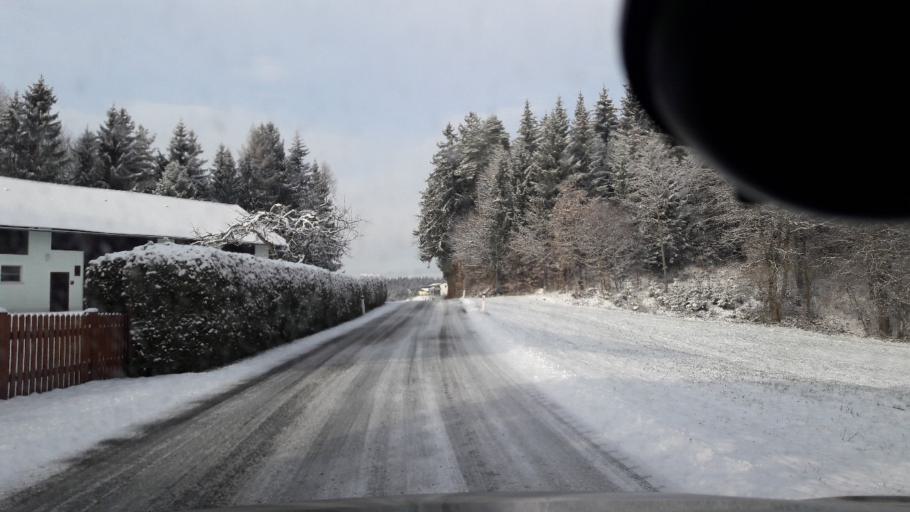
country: AT
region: Styria
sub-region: Politischer Bezirk Graz-Umgebung
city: Sankt Oswald bei Plankenwarth
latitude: 47.0921
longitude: 15.2572
